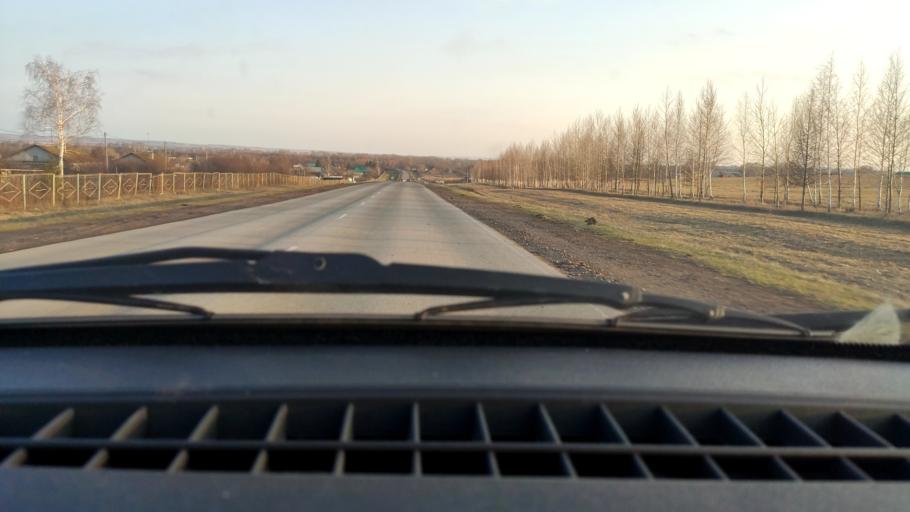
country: RU
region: Bashkortostan
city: Davlekanovo
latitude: 54.3757
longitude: 55.1955
